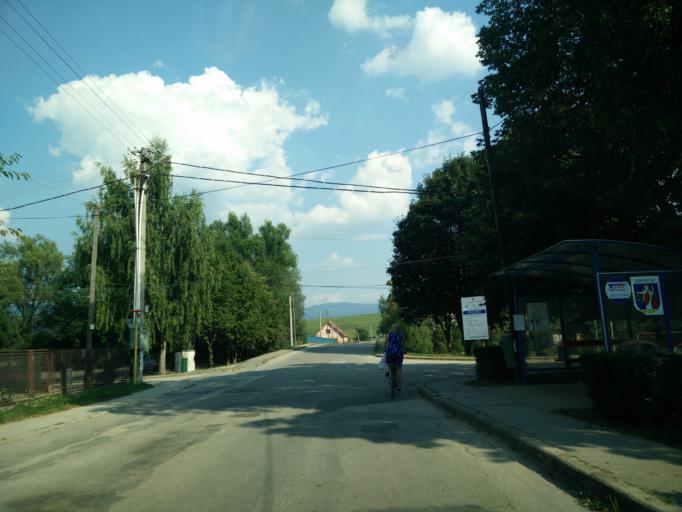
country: SK
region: Zilinsky
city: Rajec
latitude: 49.1194
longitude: 18.6508
